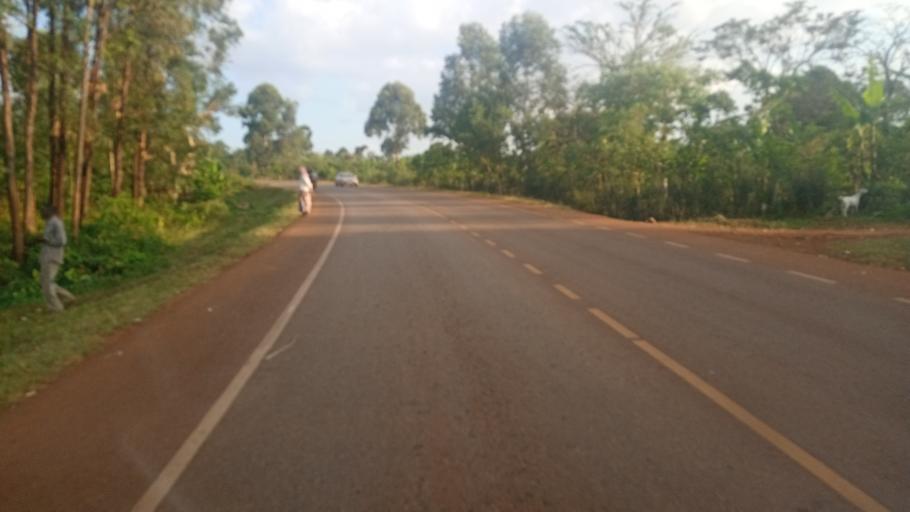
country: UG
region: Eastern Region
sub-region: Sironko District
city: Sironko
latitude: 1.3252
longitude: 34.3301
